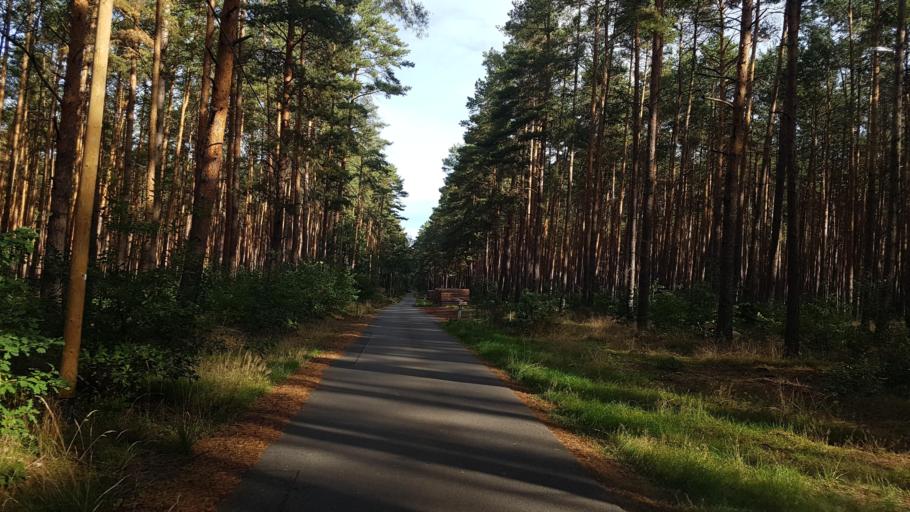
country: DE
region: Brandenburg
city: Hohenbucko
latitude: 51.8272
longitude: 13.5311
